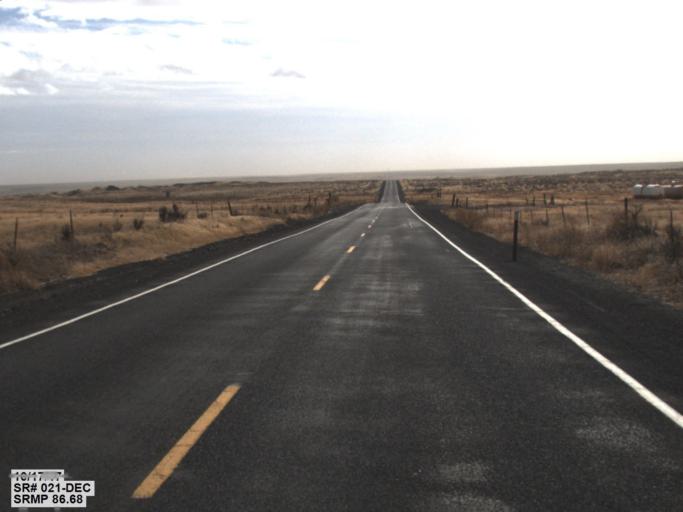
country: US
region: Washington
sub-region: Okanogan County
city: Coulee Dam
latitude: 47.6934
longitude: -118.7220
